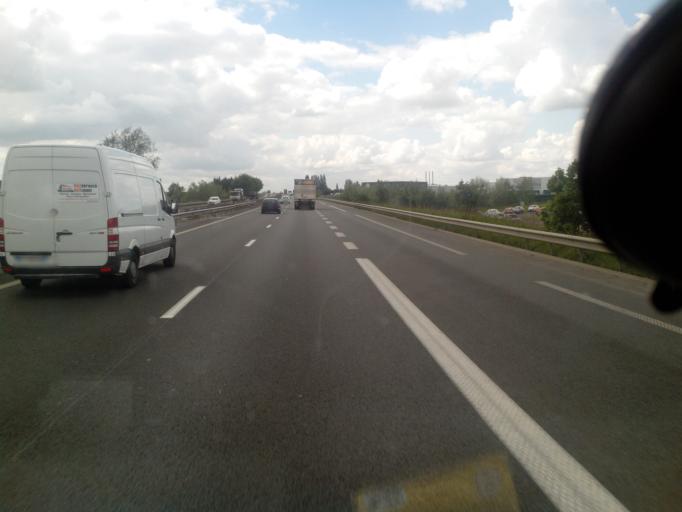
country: FR
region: Nord-Pas-de-Calais
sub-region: Departement du Nord
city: Bailleul
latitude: 50.7230
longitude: 2.7397
